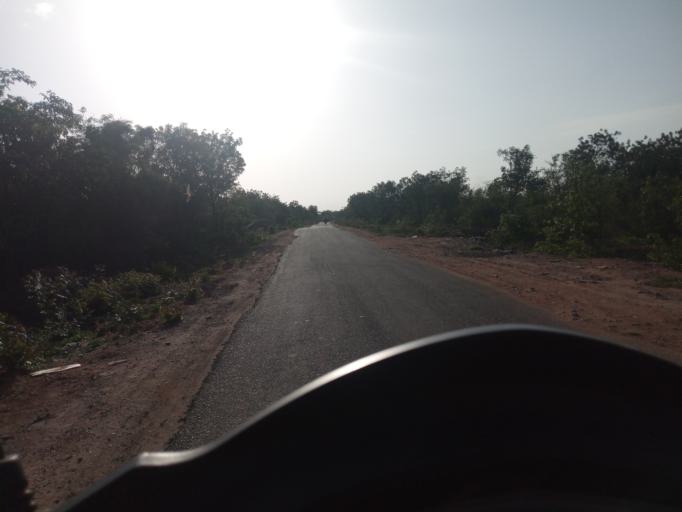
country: IN
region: Telangana
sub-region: Rangareddi
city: Quthbullapur
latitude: 17.5540
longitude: 78.4163
